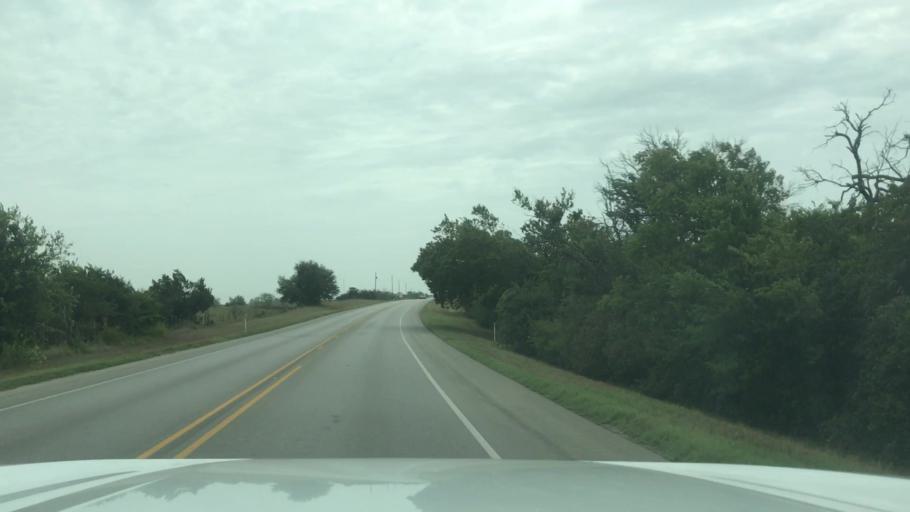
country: US
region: Texas
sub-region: Erath County
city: Dublin
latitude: 32.0971
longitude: -98.3811
